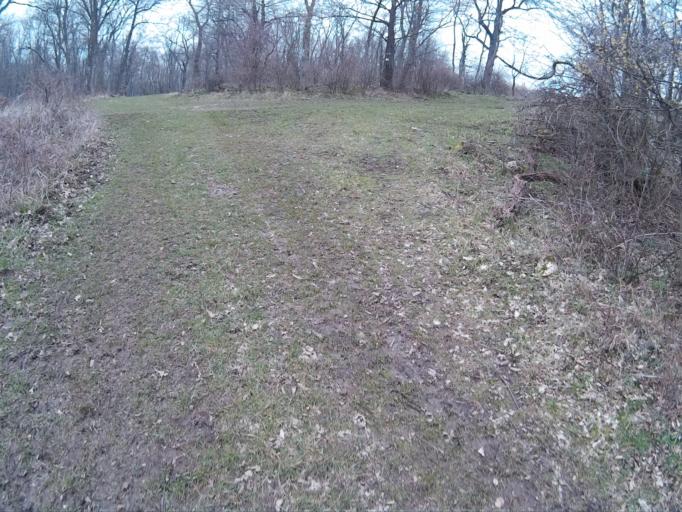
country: HU
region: Veszprem
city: Zirc
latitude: 47.1777
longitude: 17.8733
